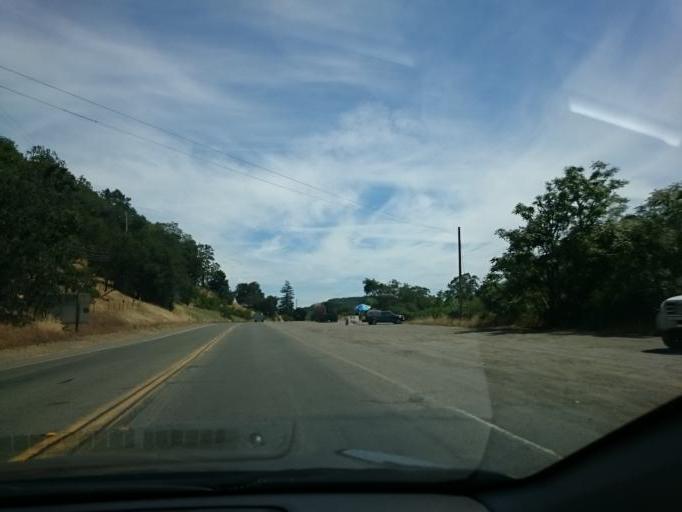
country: US
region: California
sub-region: Sonoma County
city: Healdsburg
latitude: 38.6498
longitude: -122.8690
